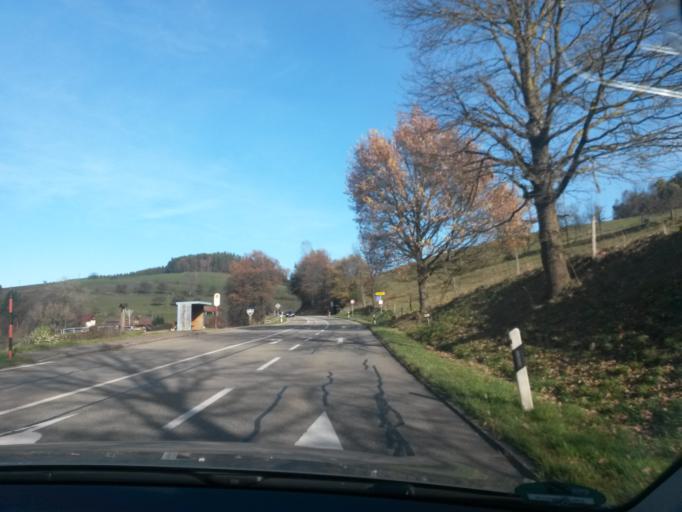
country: DE
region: Baden-Wuerttemberg
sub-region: Freiburg Region
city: Elzach
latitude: 48.1983
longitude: 8.0823
